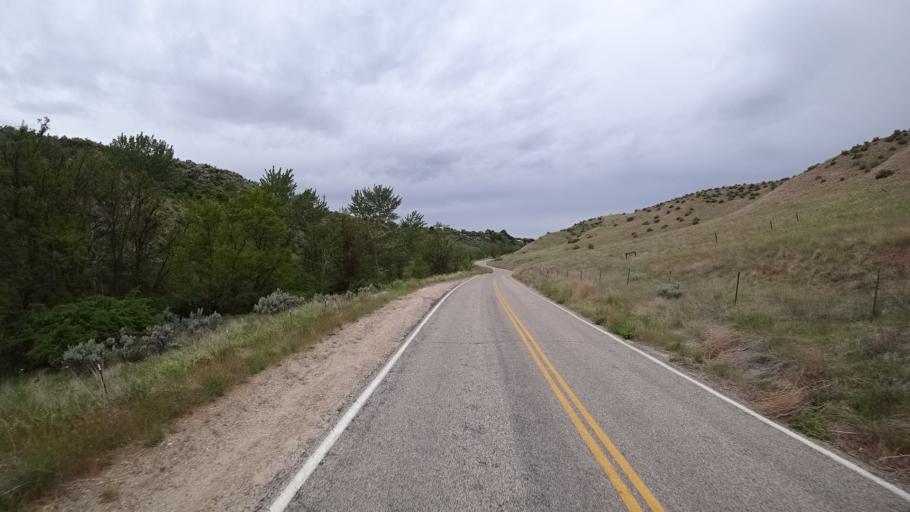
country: US
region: Idaho
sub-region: Ada County
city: Boise
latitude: 43.6165
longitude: -116.1528
